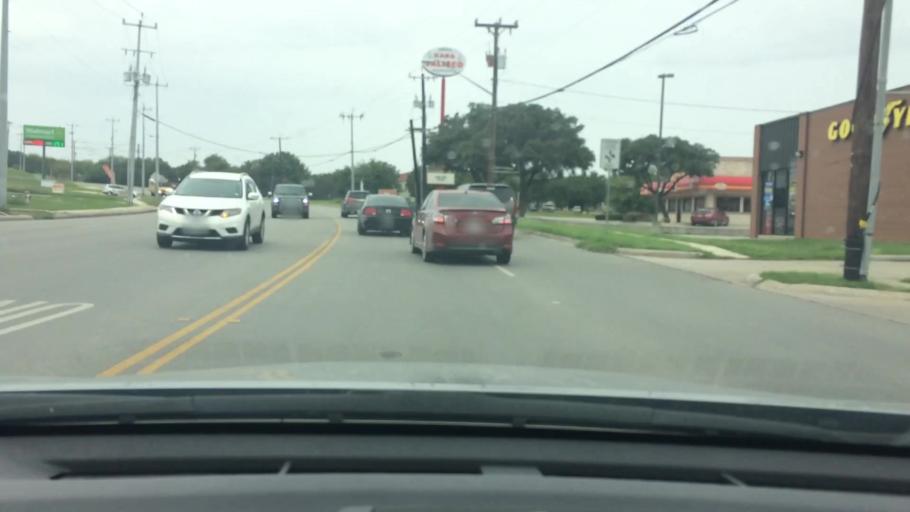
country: US
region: Texas
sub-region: Bexar County
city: Converse
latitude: 29.5358
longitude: -98.3313
